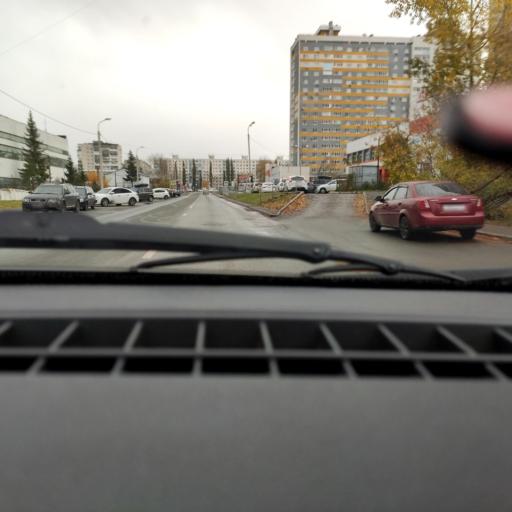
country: RU
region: Bashkortostan
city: Ufa
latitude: 54.7846
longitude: 56.1183
